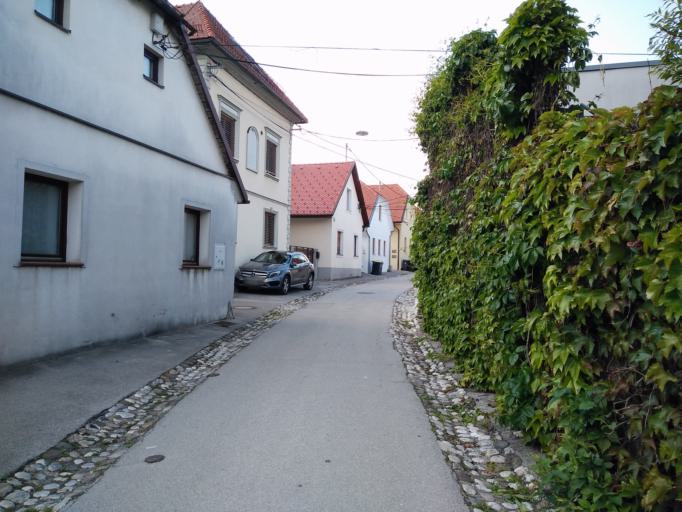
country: SI
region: Ljubljana
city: Ljubljana
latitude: 46.0441
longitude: 14.5041
